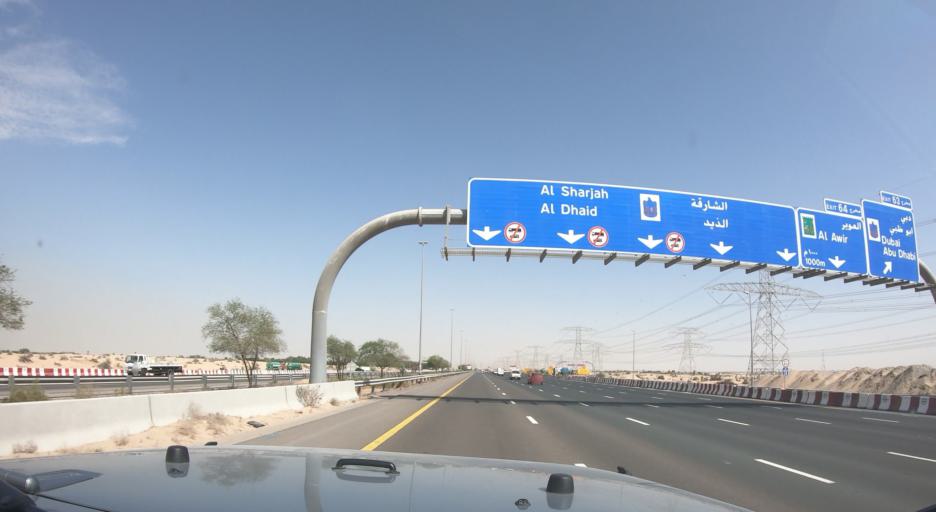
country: AE
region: Ash Shariqah
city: Sharjah
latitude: 25.1831
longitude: 55.5221
